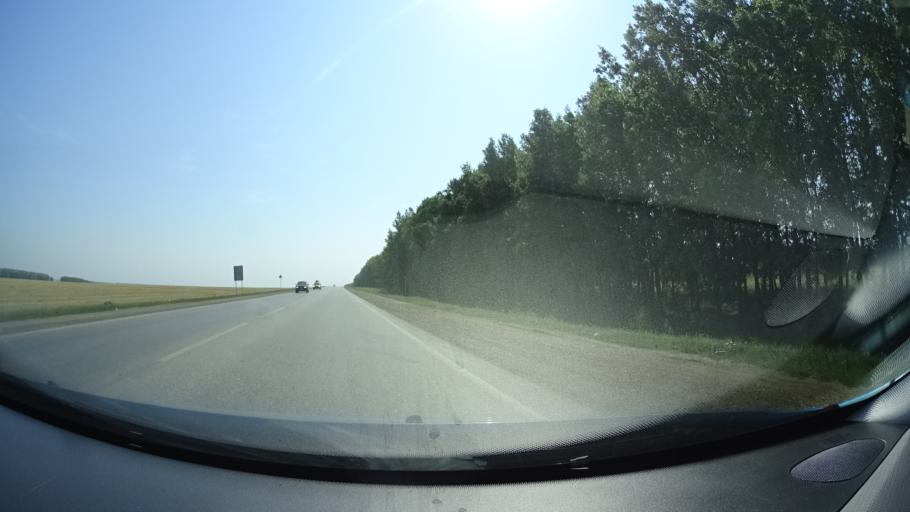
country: RU
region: Bashkortostan
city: Kabakovo
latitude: 54.4752
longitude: 55.9361
